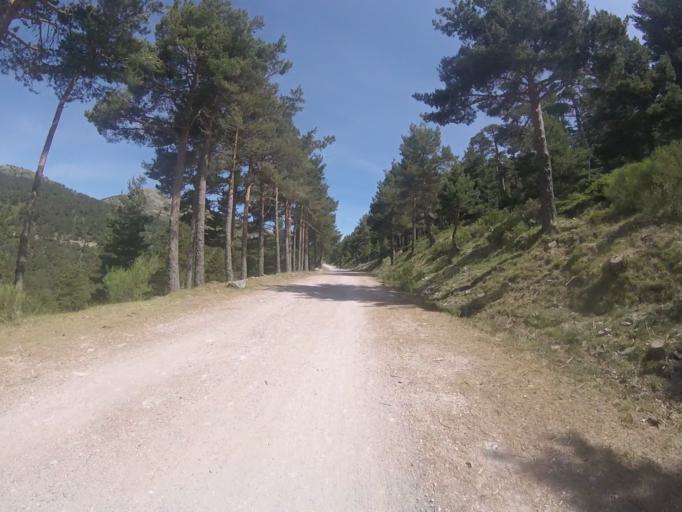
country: ES
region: Madrid
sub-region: Provincia de Madrid
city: Cercedilla
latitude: 40.7897
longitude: -4.0591
